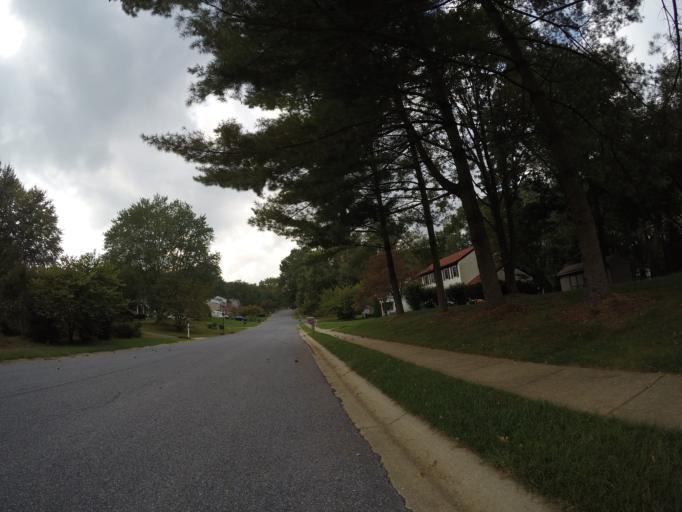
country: US
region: Maryland
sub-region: Howard County
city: Columbia
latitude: 39.2571
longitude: -76.8619
